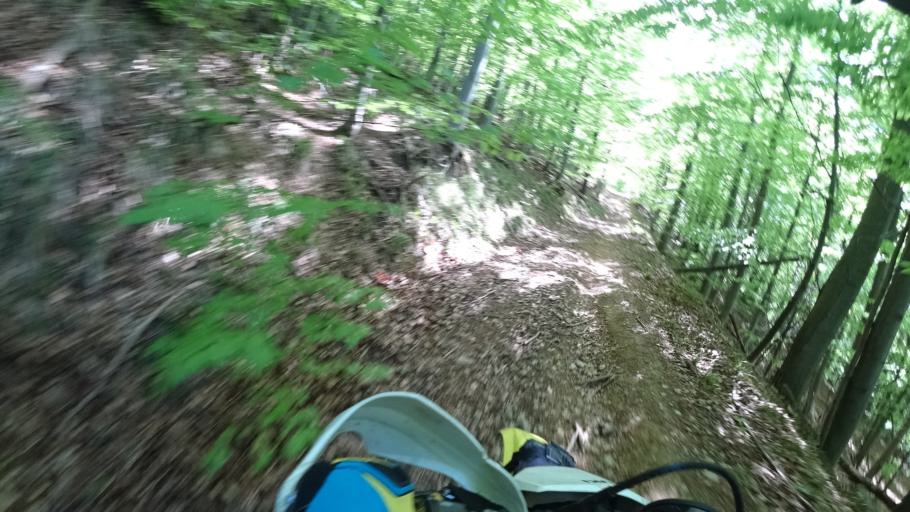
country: HR
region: Zagrebacka
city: Jablanovec
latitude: 45.8731
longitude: 15.9023
